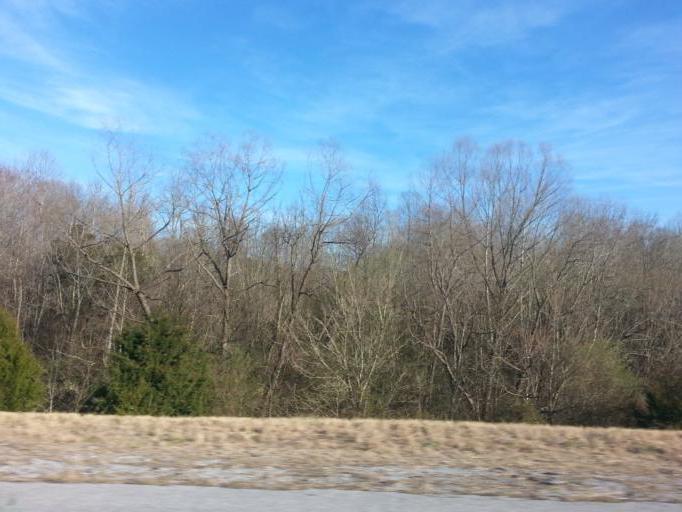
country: US
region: Tennessee
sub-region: White County
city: Sparta
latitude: 35.8414
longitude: -85.5109
